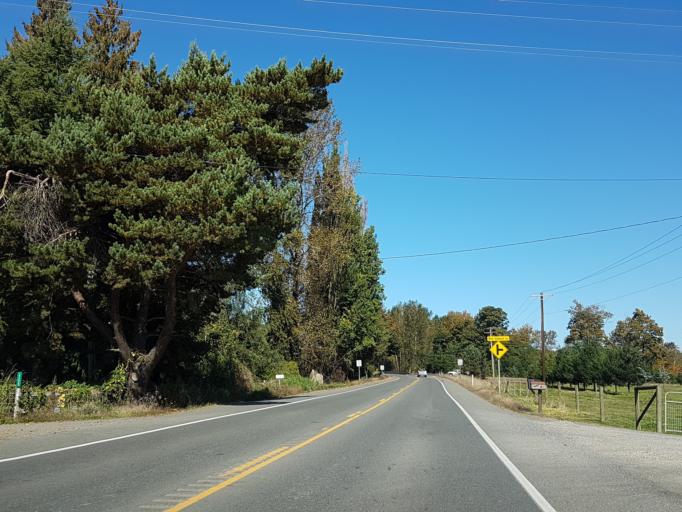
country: US
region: Washington
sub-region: Snohomish County
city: Monroe
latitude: 47.8410
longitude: -121.9693
